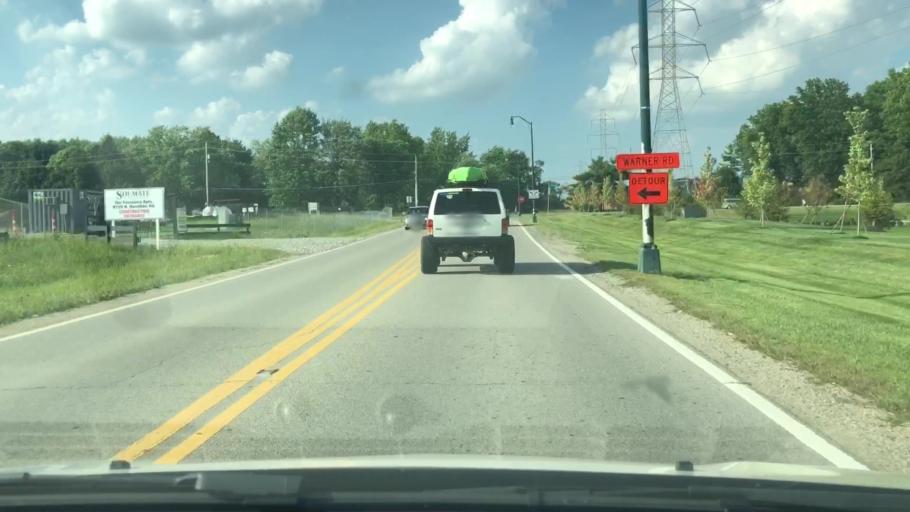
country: US
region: Ohio
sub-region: Franklin County
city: New Albany
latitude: 40.0986
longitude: -82.8486
